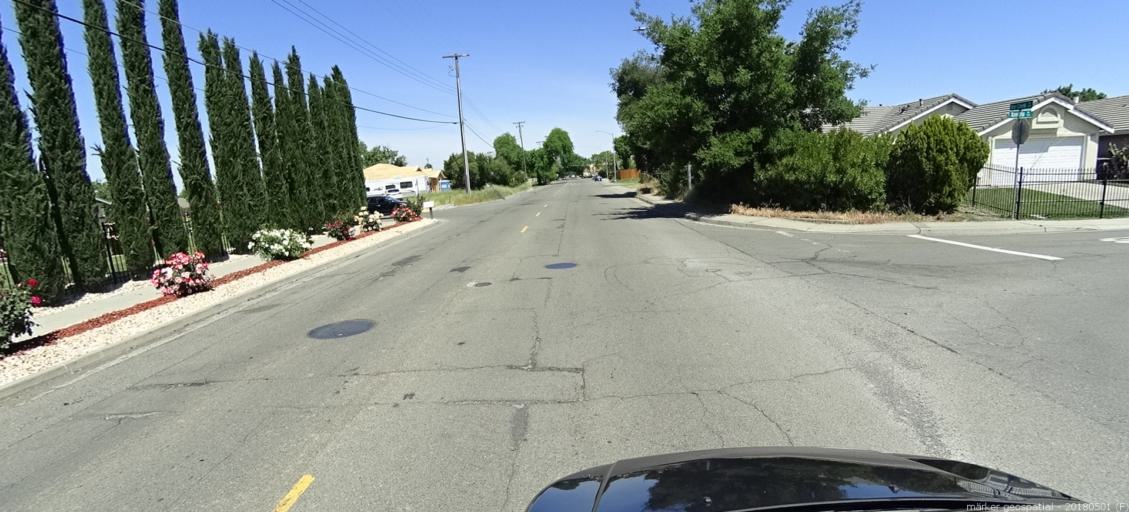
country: US
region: California
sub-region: Sacramento County
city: Rio Linda
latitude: 38.6452
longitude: -121.4384
